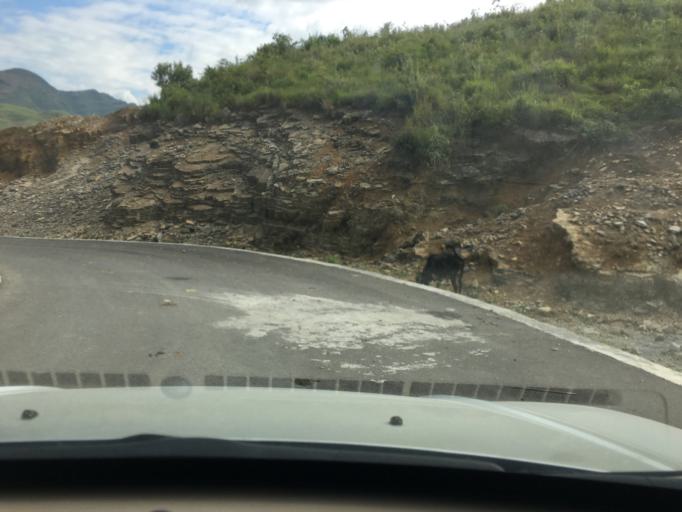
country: CN
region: Guizhou Sheng
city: Anshun
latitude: 25.7776
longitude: 105.3799
